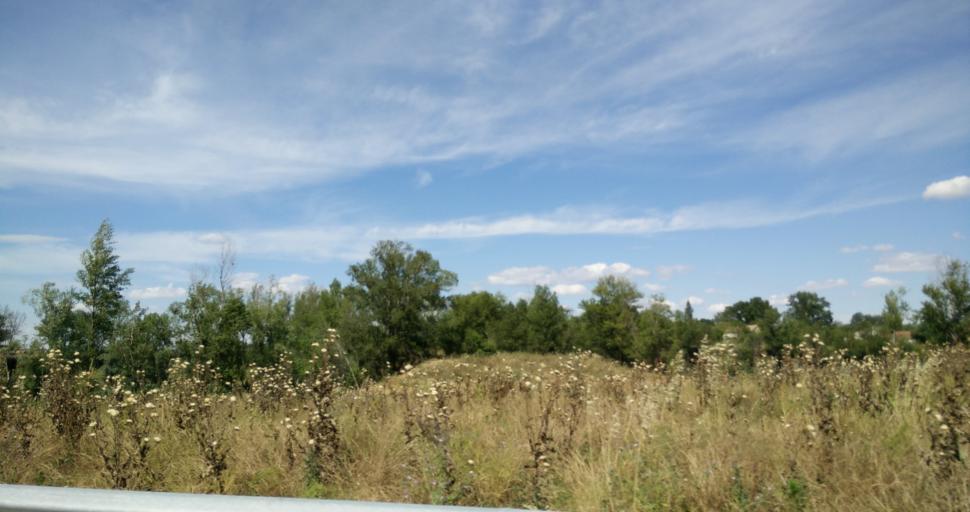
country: FR
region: Languedoc-Roussillon
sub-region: Departement du Gard
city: Vestric-et-Candiac
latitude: 43.7222
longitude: 4.2577
